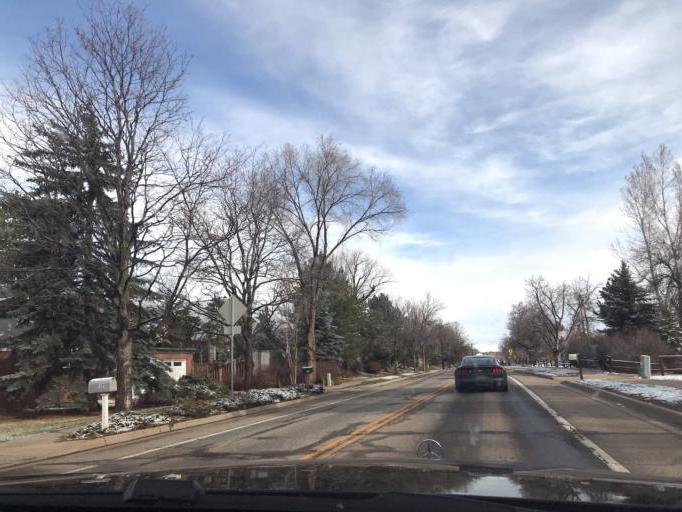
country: US
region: Colorado
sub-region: Boulder County
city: Boulder
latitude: 40.0113
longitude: -105.2253
